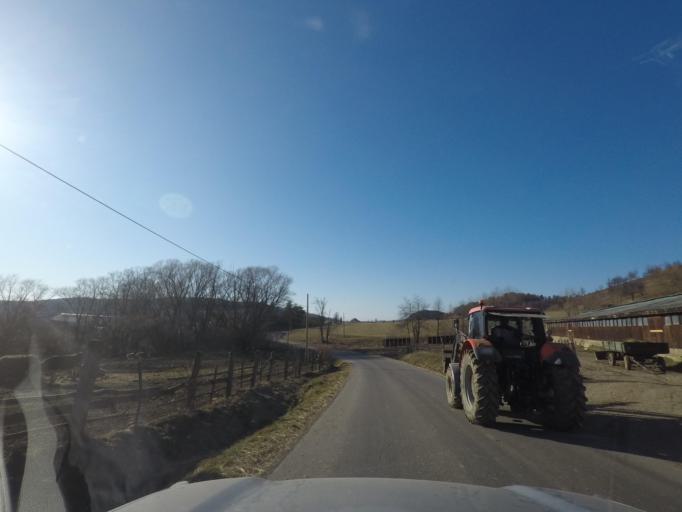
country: SK
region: Presovsky
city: Medzilaborce
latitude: 49.2200
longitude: 21.9796
